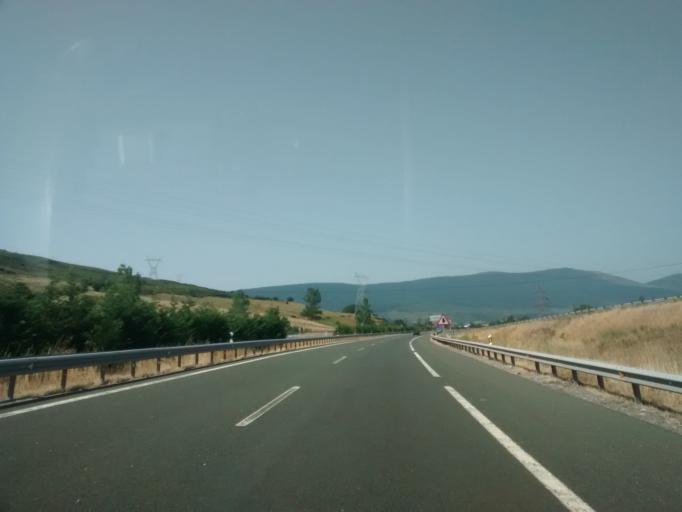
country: ES
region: Cantabria
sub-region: Provincia de Cantabria
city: Reinosa
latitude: 42.9849
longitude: -4.1347
